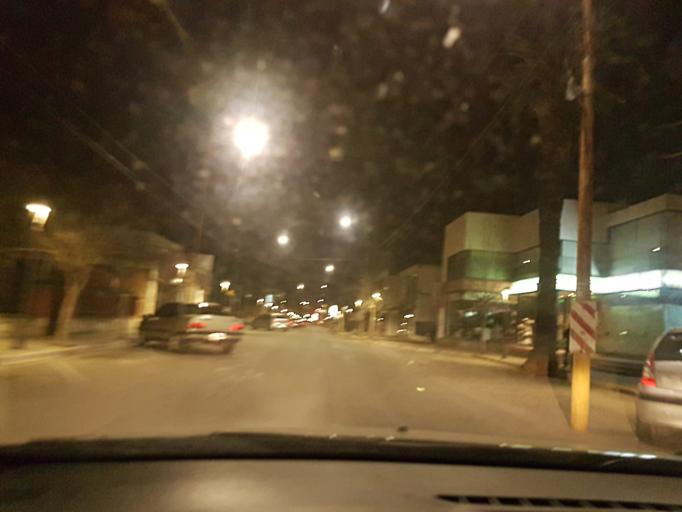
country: AR
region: Cordoba
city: Villa Allende
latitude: -31.2938
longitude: -64.2927
